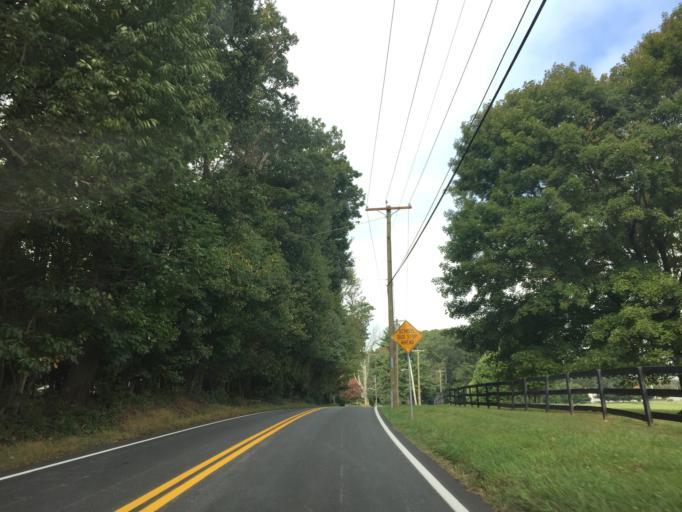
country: US
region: Maryland
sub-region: Baltimore County
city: Mays Chapel
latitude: 39.4362
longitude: -76.7089
